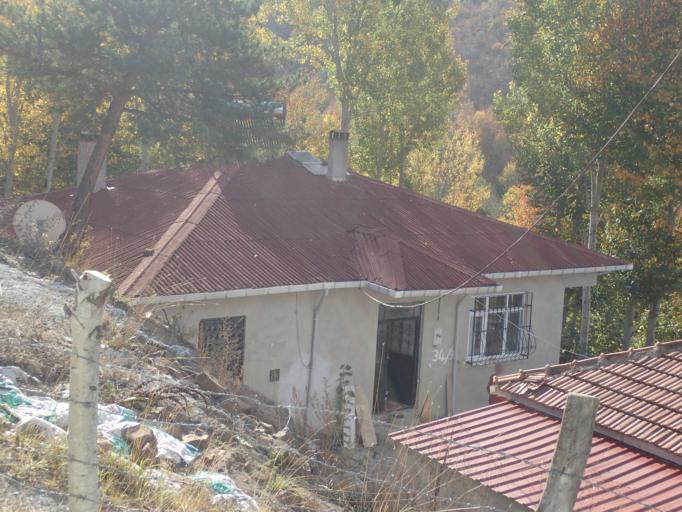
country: TR
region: Ordu
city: Topcam
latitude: 40.5777
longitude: 37.7096
